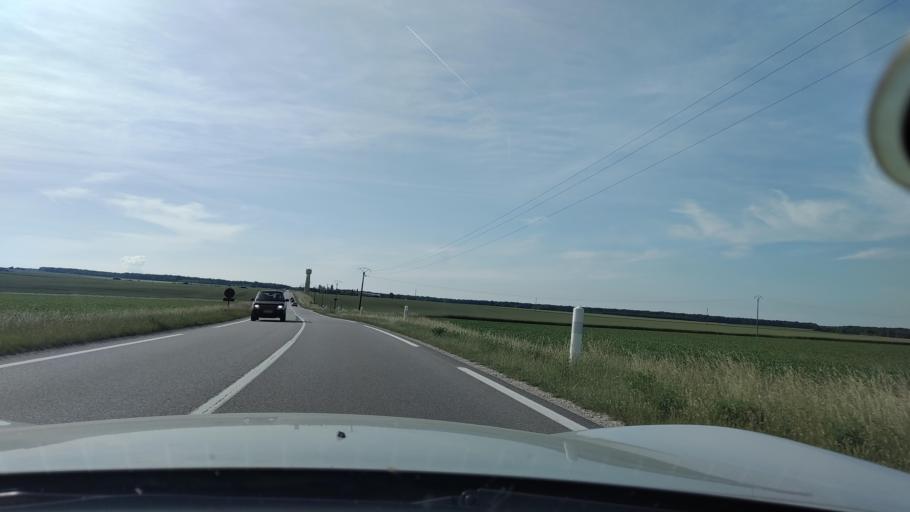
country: FR
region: Ile-de-France
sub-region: Departement de Seine-et-Marne
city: Jouy-le-Chatel
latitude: 48.6610
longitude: 3.1407
